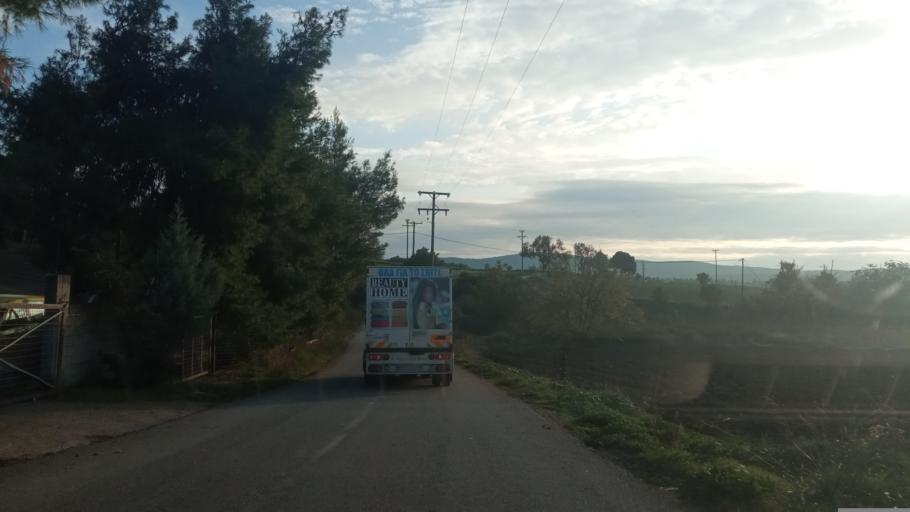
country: GR
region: Central Greece
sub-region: Nomos Evvoias
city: Psachna
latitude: 38.5775
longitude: 23.7114
